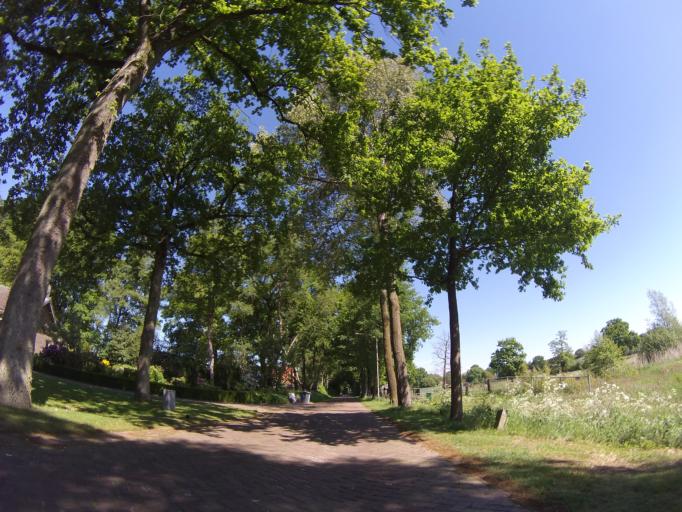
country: NL
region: Drenthe
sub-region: Gemeente Coevorden
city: Sleen
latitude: 52.7894
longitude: 6.7256
